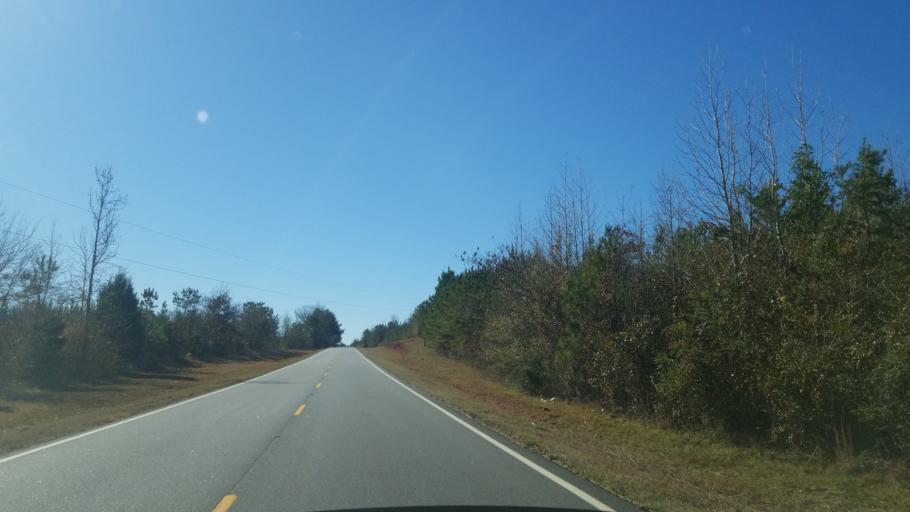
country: US
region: Georgia
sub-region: Talbot County
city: Sardis
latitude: 32.6404
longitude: -84.7128
